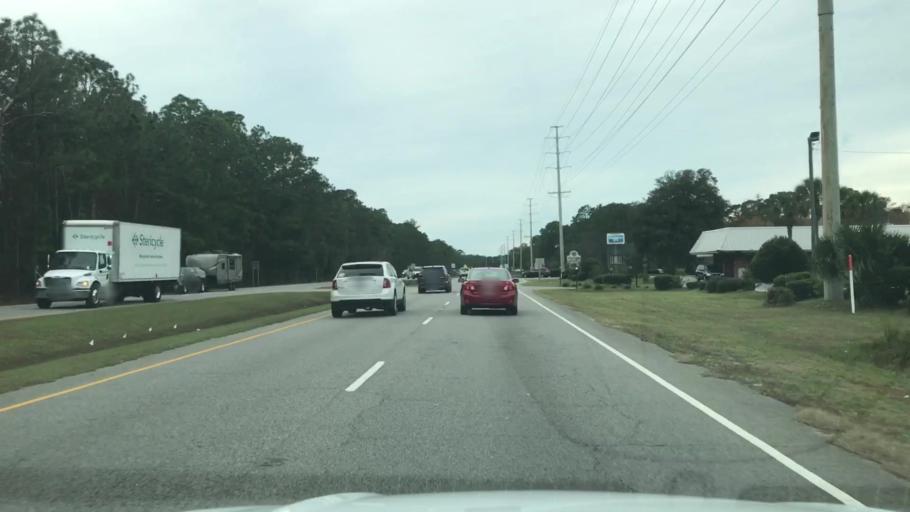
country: US
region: South Carolina
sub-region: Georgetown County
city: Georgetown
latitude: 33.4230
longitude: -79.1669
